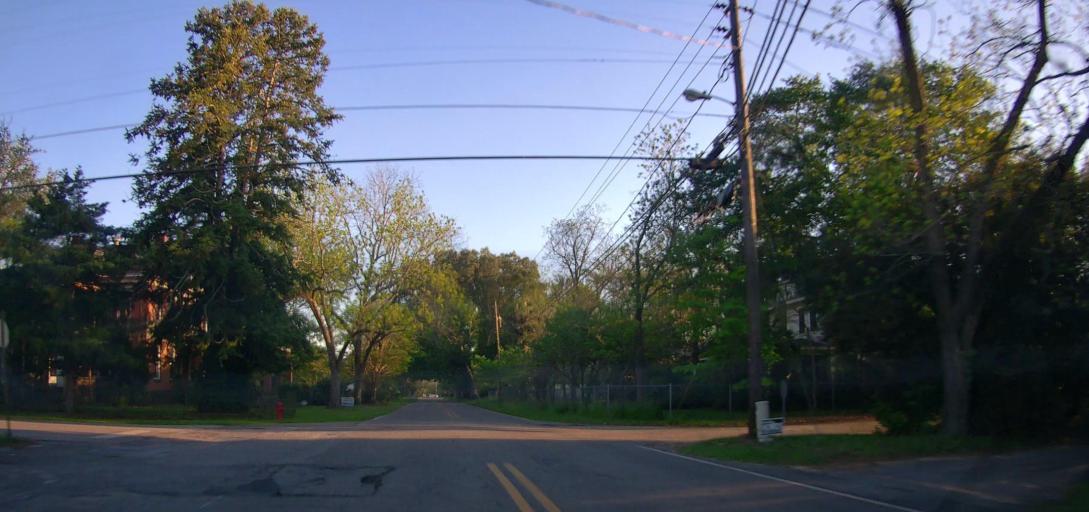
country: US
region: Georgia
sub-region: Irwin County
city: Ocilla
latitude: 31.5970
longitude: -83.2591
